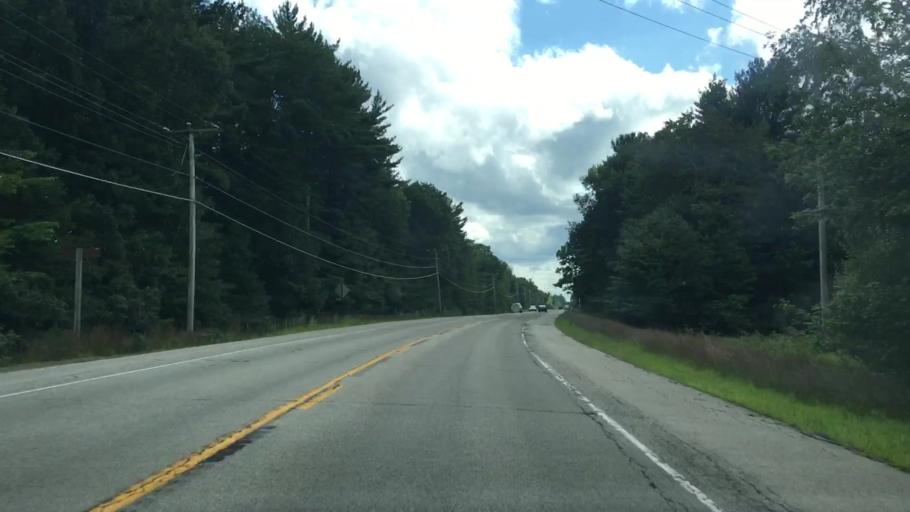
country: US
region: Maine
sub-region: York County
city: South Sanford
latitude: 43.3984
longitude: -70.7391
